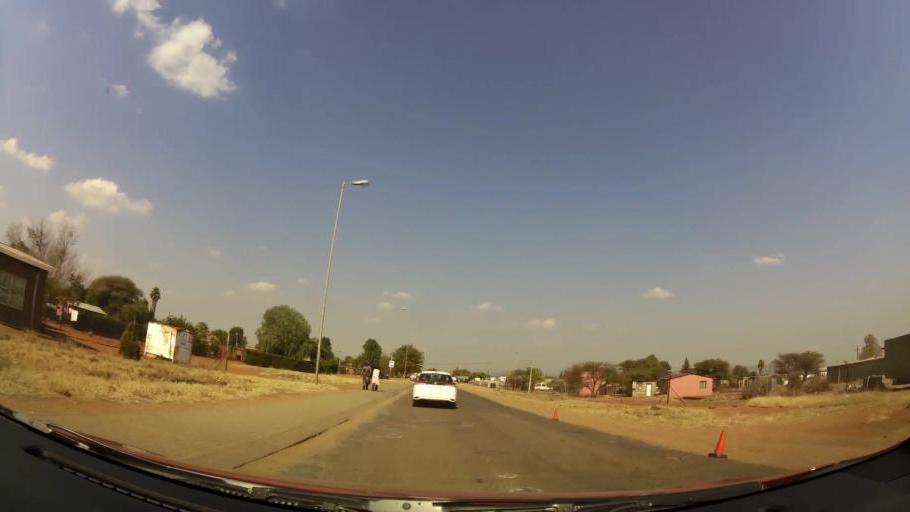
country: ZA
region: North-West
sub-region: Bojanala Platinum District Municipality
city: Mogwase
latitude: -25.3716
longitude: 27.0633
